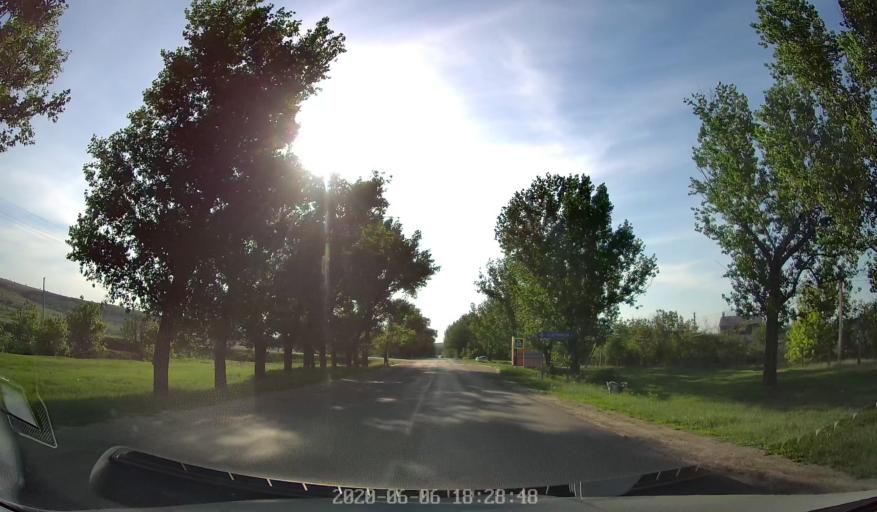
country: MD
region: Chisinau
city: Ciorescu
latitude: 47.1294
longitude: 28.9801
